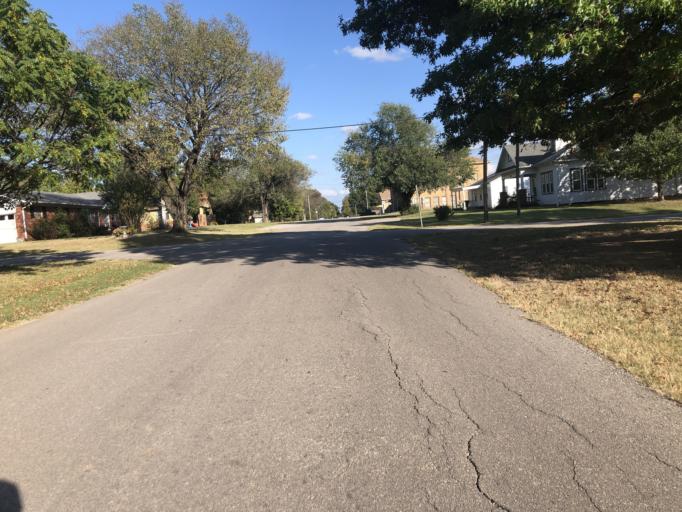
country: US
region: Oklahoma
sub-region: Pottawatomie County
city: Tecumseh
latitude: 35.2555
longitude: -96.9384
